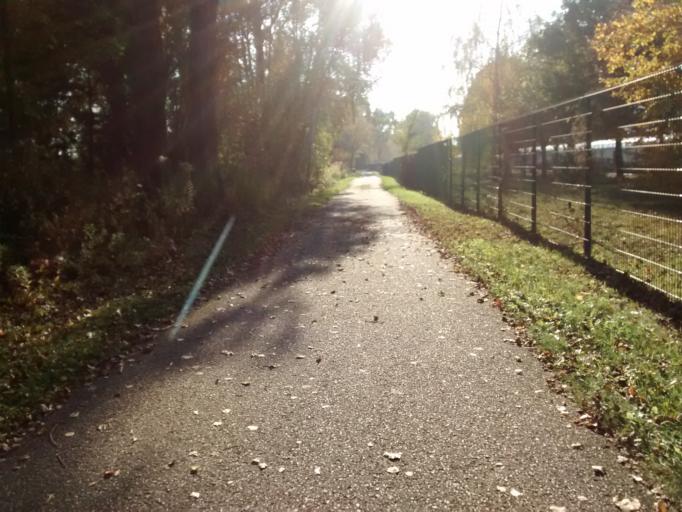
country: DE
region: Brandenburg
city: Hennigsdorf
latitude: 52.6204
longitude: 13.2115
